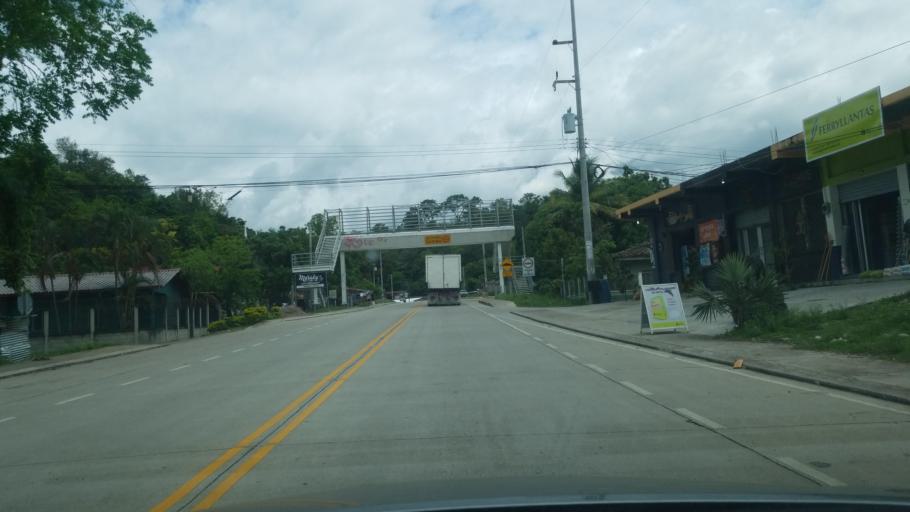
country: HN
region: Copan
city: Florida
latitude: 15.0262
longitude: -88.8322
